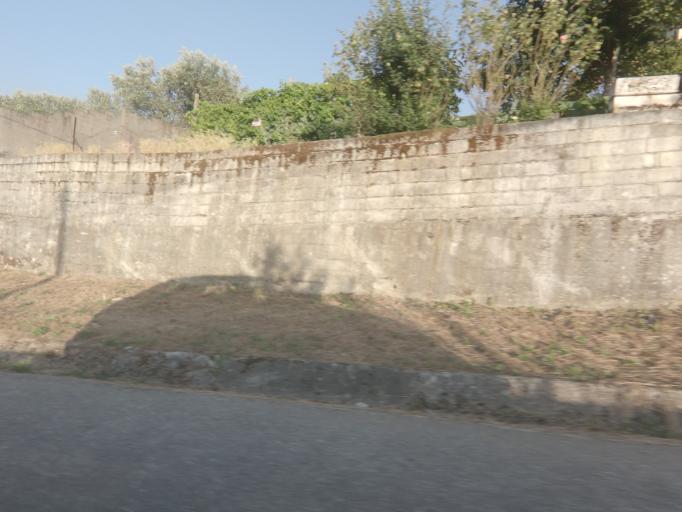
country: PT
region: Viseu
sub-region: Armamar
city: Armamar
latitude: 41.1901
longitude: -7.6876
